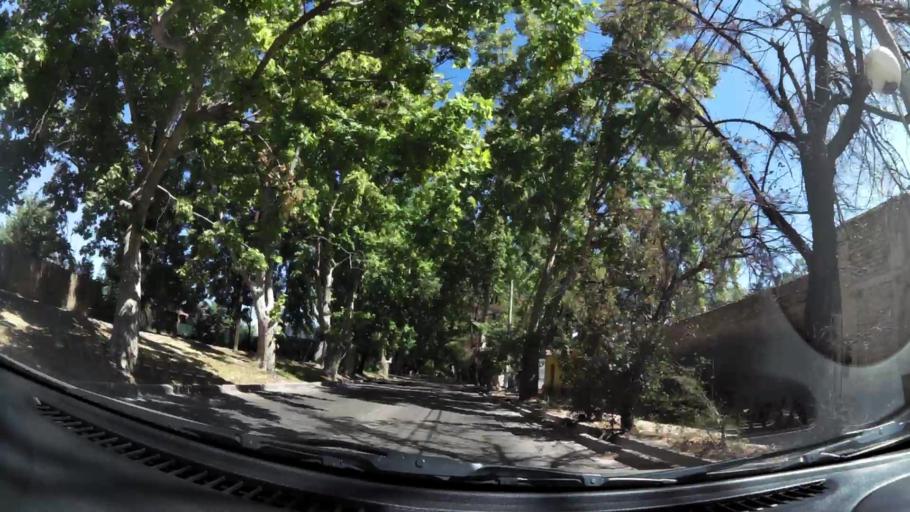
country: AR
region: Mendoza
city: Lujan de Cuyo
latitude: -32.9850
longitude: -68.8611
